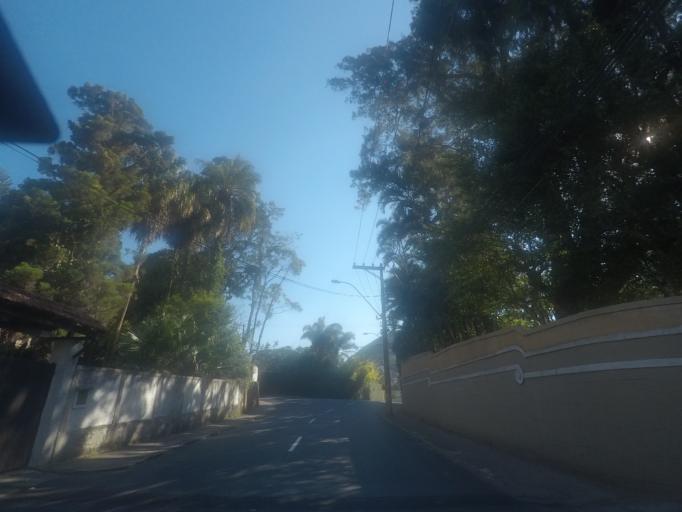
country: BR
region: Rio de Janeiro
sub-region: Petropolis
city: Petropolis
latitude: -22.5132
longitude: -43.1673
